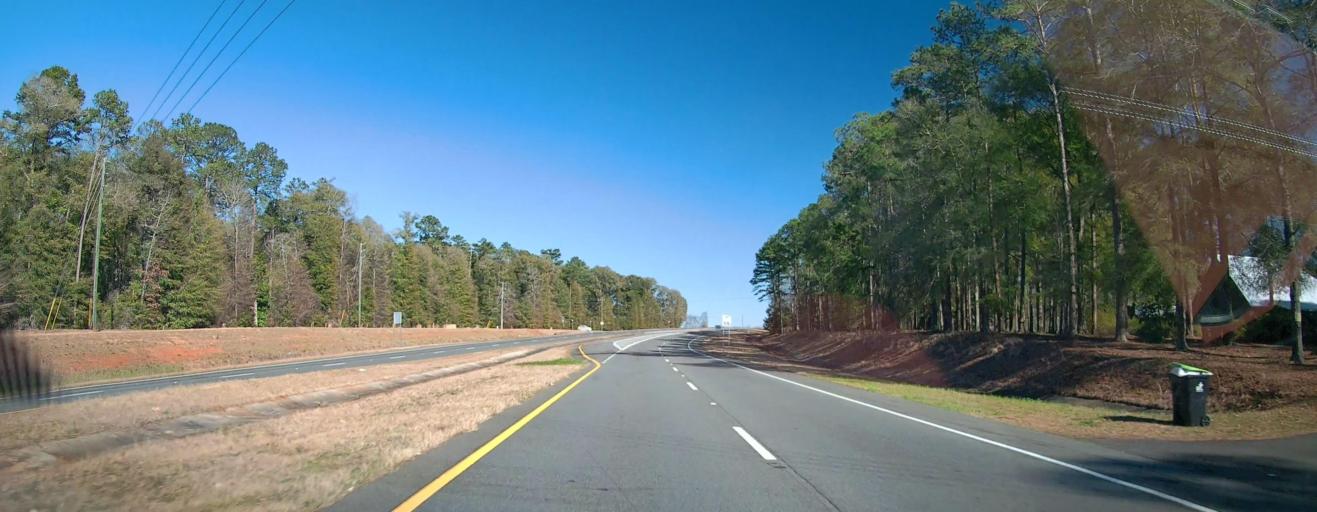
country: US
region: Georgia
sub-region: Sumter County
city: Americus
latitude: 32.1145
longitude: -84.2526
